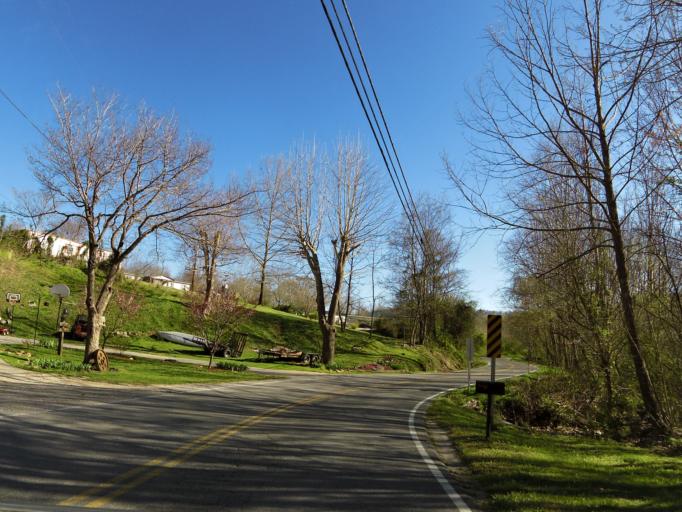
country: US
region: Tennessee
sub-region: Scott County
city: Huntsville
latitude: 36.3399
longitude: -84.3860
